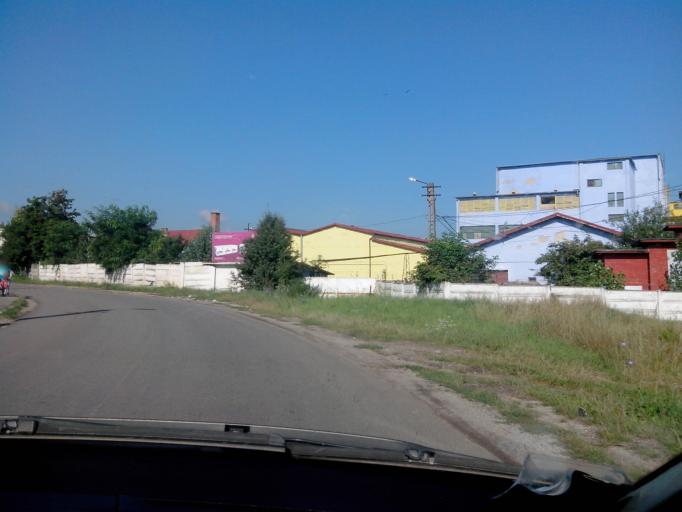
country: RO
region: Cluj
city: Aghiresu-Fabricei
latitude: 46.8665
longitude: 23.2751
